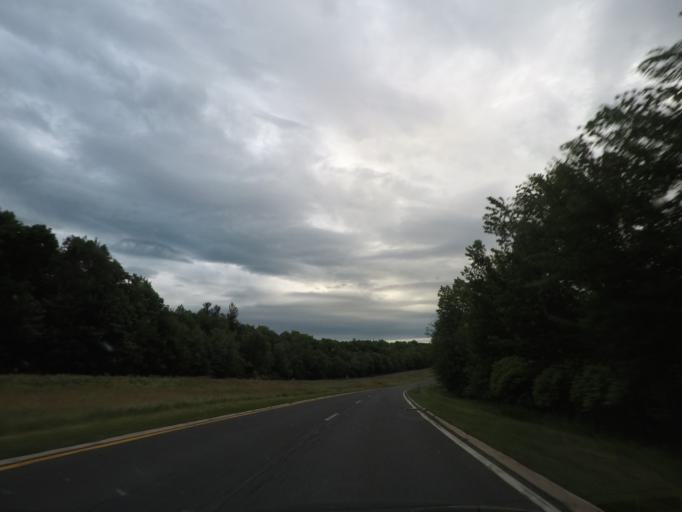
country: US
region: New York
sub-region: Columbia County
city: Philmont
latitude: 42.1830
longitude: -73.6594
